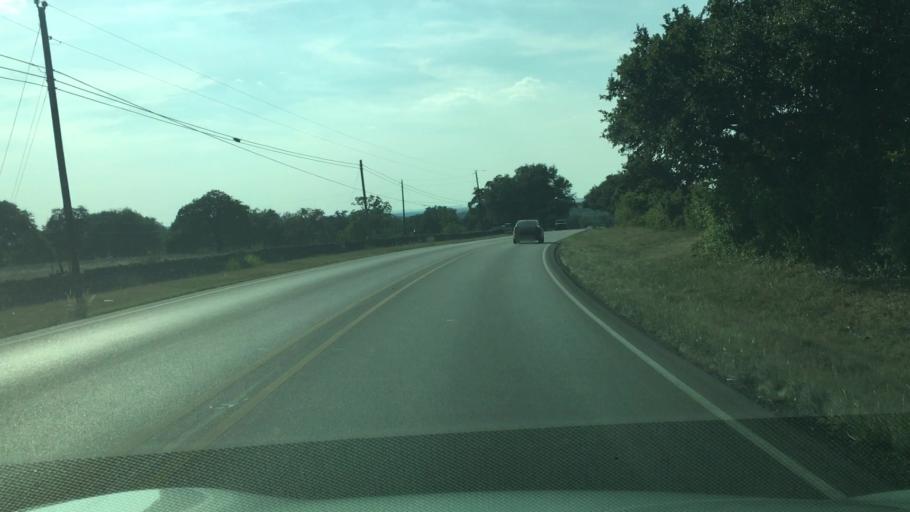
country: US
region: Texas
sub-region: Hays County
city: Dripping Springs
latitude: 30.1177
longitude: -97.9870
